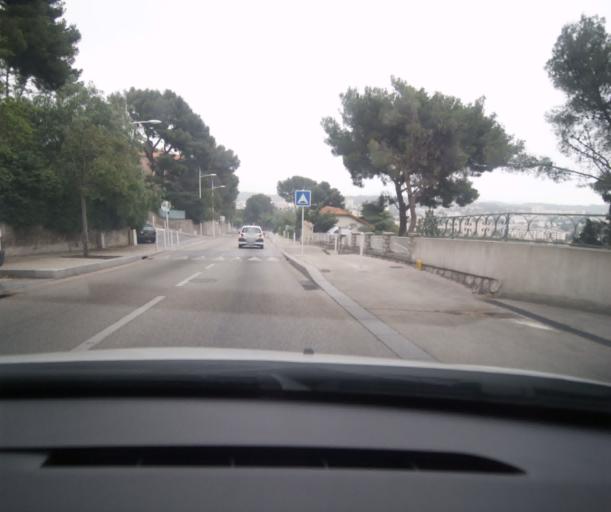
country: FR
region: Provence-Alpes-Cote d'Azur
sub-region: Departement du Var
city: La Valette-du-Var
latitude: 43.1342
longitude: 5.9720
